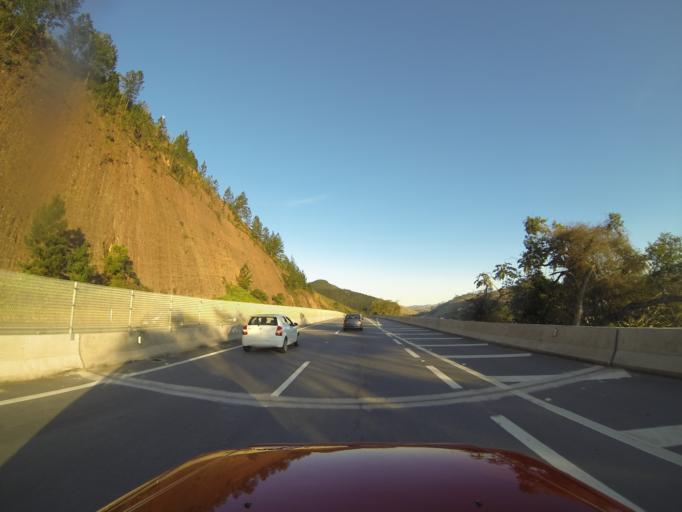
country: BR
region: Sao Paulo
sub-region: Santa Branca
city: Santa Branca
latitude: -23.3846
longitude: -45.6608
